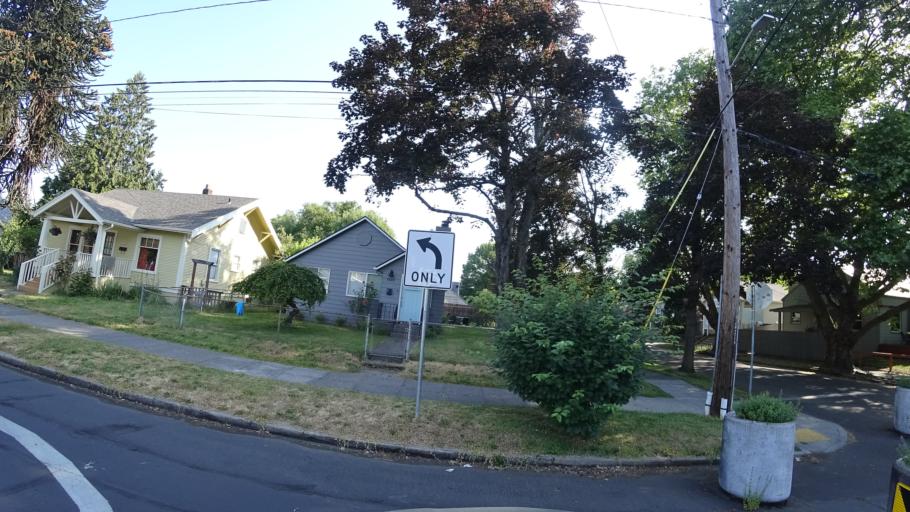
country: US
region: Oregon
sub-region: Washington County
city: West Haven
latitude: 45.5902
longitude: -122.7460
